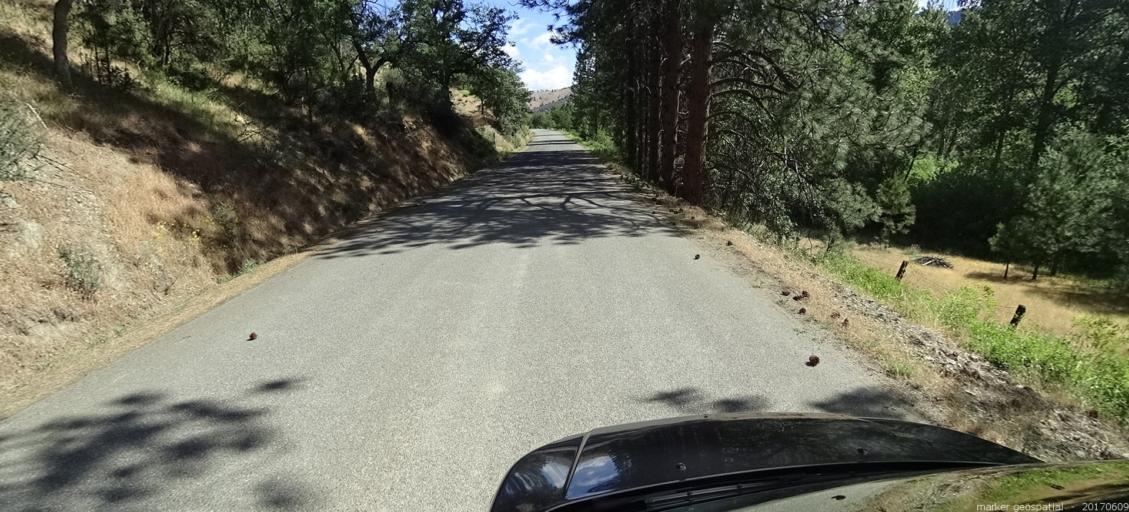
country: US
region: California
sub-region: Siskiyou County
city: Yreka
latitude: 41.3367
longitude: -122.8282
